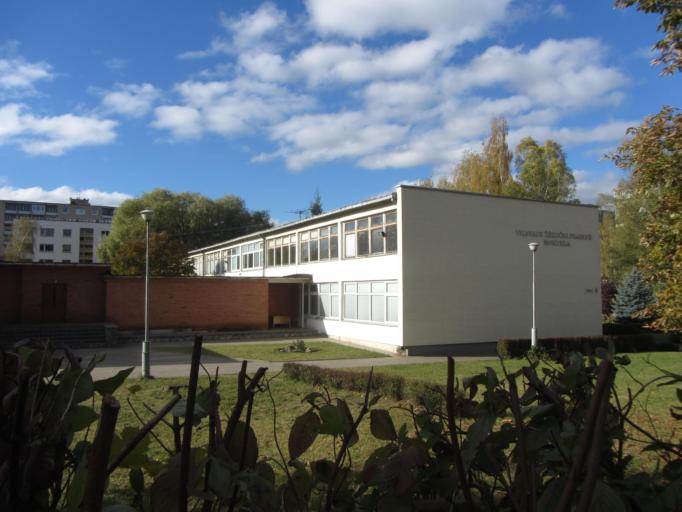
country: LT
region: Vilnius County
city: Lazdynai
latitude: 54.6742
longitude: 25.2098
